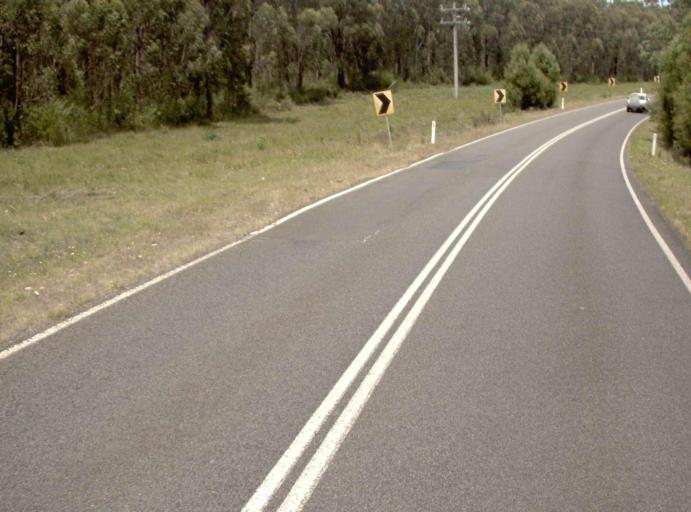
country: AU
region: Victoria
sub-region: Latrobe
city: Moe
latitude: -38.0653
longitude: 146.3362
